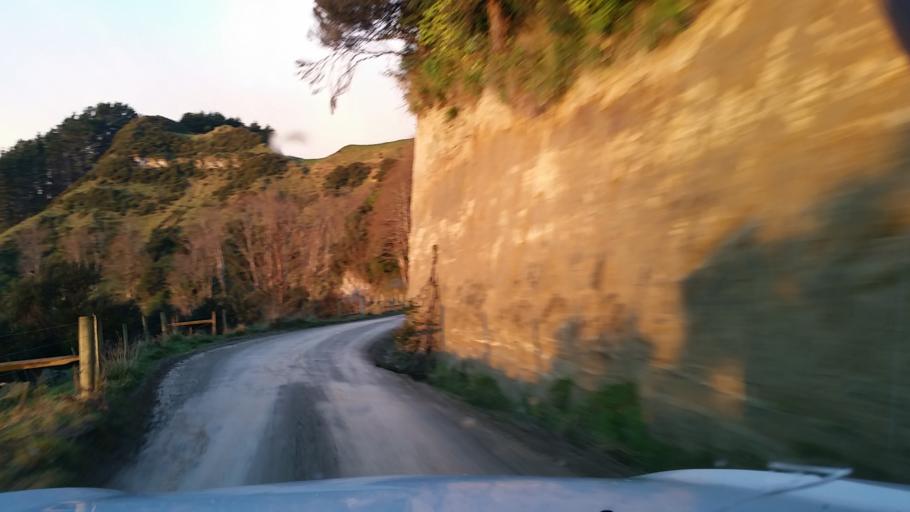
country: NZ
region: Manawatu-Wanganui
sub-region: Wanganui District
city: Wanganui
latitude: -39.7656
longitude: 174.8735
